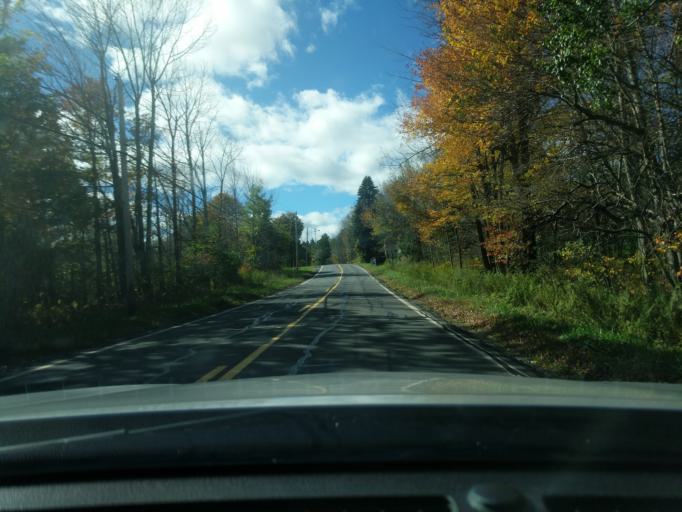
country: US
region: Massachusetts
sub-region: Berkshire County
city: Otis
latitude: 42.1724
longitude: -73.0033
